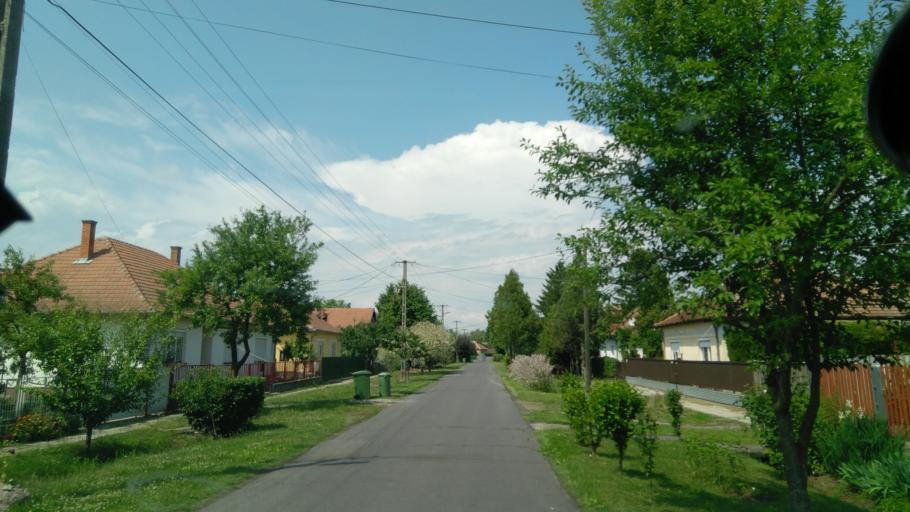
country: HU
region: Bekes
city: Bekes
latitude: 46.7620
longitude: 21.1477
